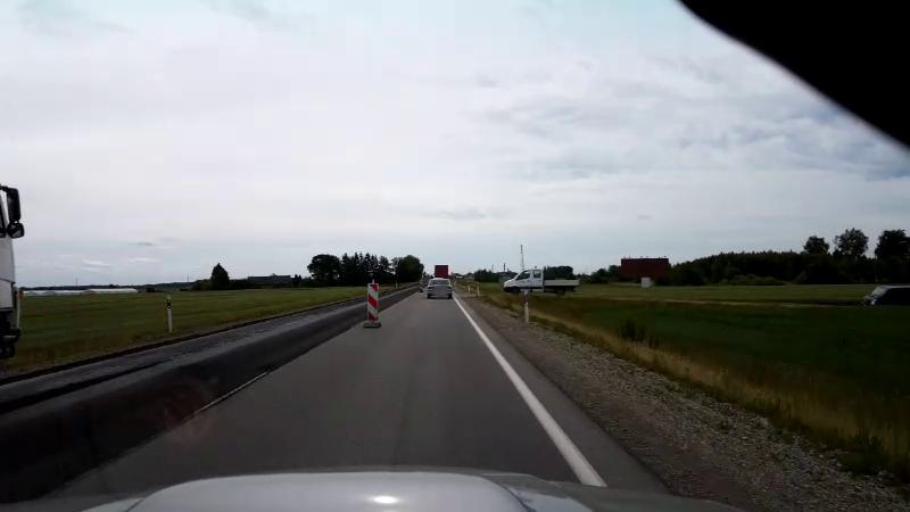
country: LV
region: Bauskas Rajons
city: Bauska
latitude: 56.2837
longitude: 24.3594
